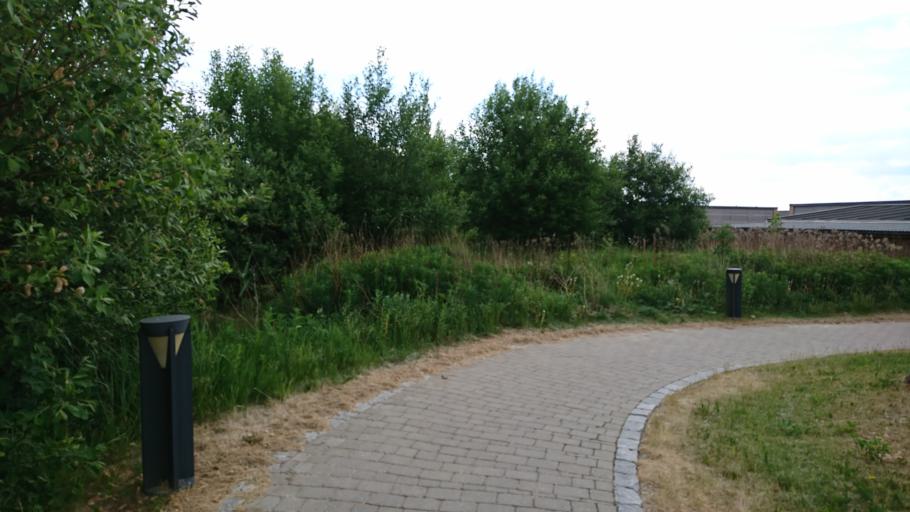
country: DK
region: Capital Region
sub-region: Ballerup Kommune
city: Ballerup
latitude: 55.7371
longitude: 12.4005
